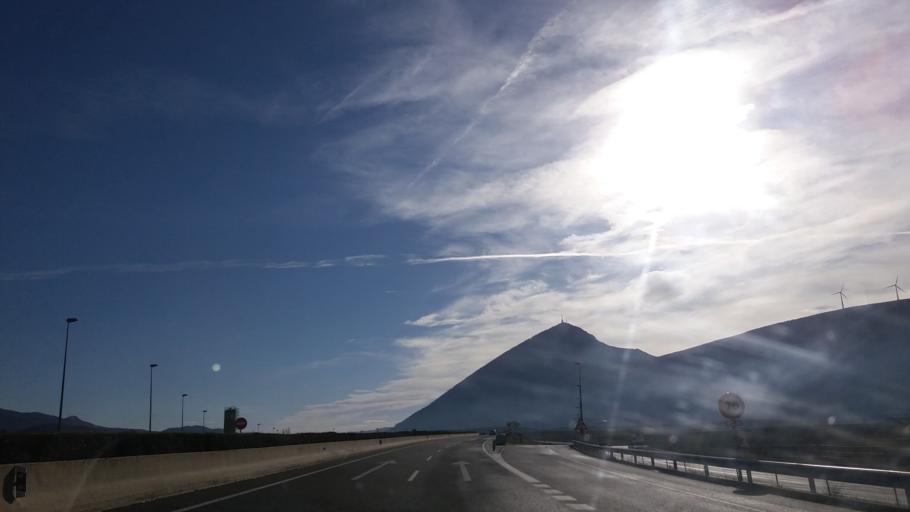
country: ES
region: Navarre
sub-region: Provincia de Navarra
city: Elorz
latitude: 42.7342
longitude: -1.5699
